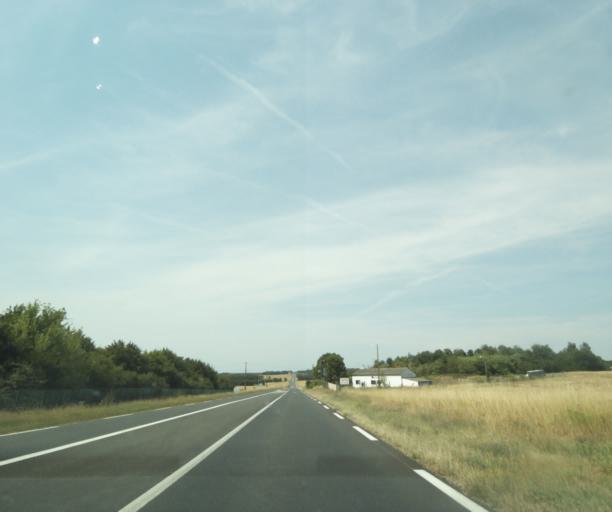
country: FR
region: Centre
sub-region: Departement d'Indre-et-Loire
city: Sainte-Maure-de-Touraine
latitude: 47.0733
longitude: 0.6137
